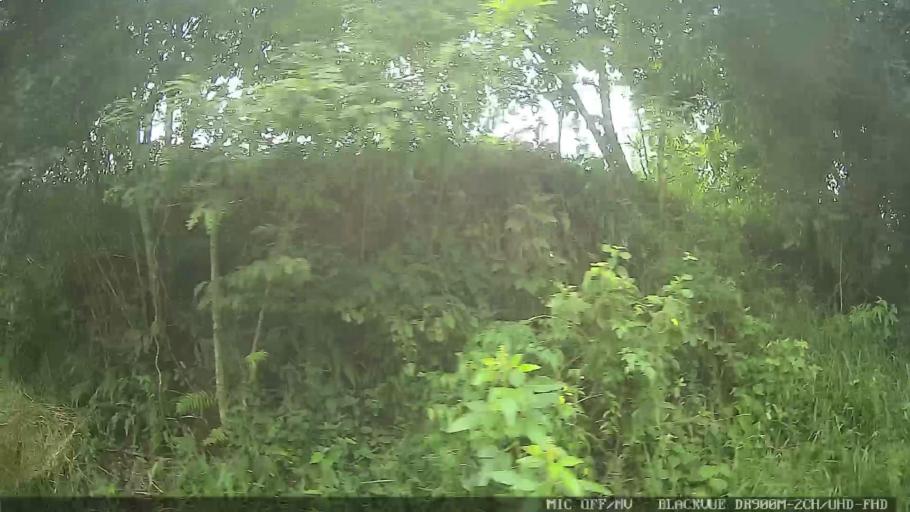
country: BR
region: Sao Paulo
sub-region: Santa Isabel
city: Santa Isabel
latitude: -23.3369
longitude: -46.2243
